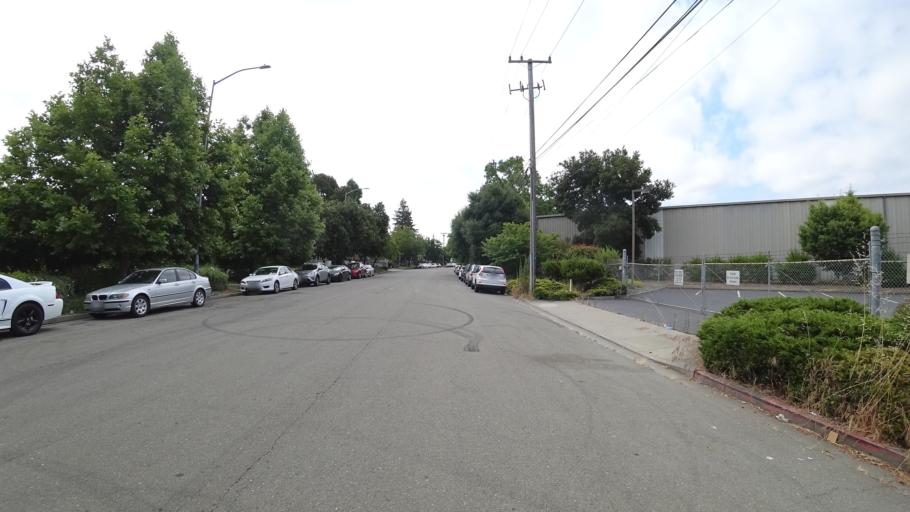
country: US
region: California
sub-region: Alameda County
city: Union City
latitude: 37.6137
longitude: -122.0462
